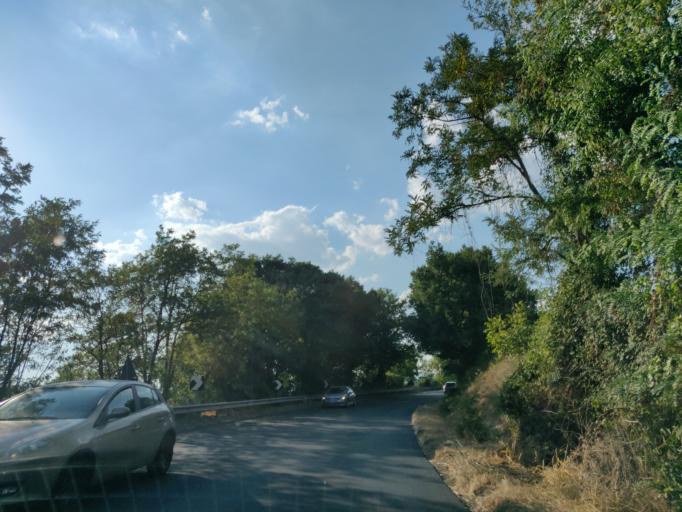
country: IT
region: Latium
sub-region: Provincia di Viterbo
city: Proceno
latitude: 42.7816
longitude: 11.8332
